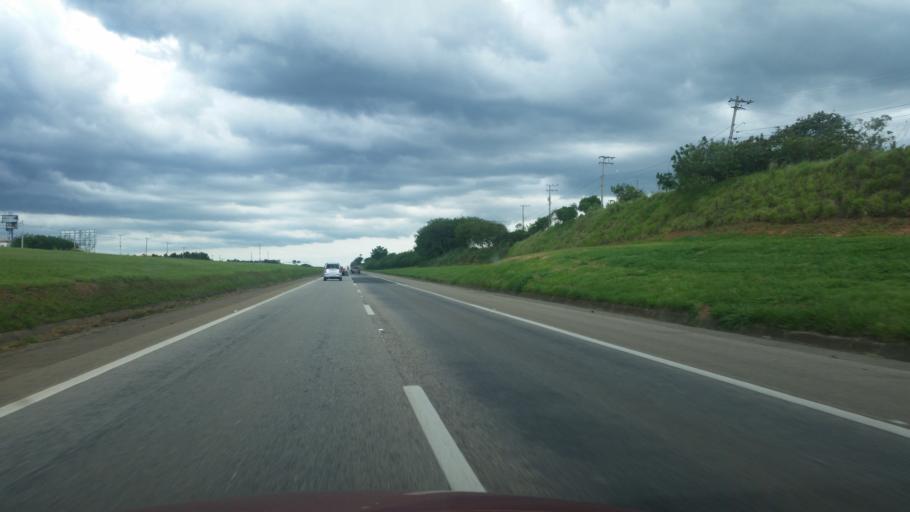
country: BR
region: Sao Paulo
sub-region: Boituva
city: Boituva
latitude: -23.3182
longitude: -47.6279
